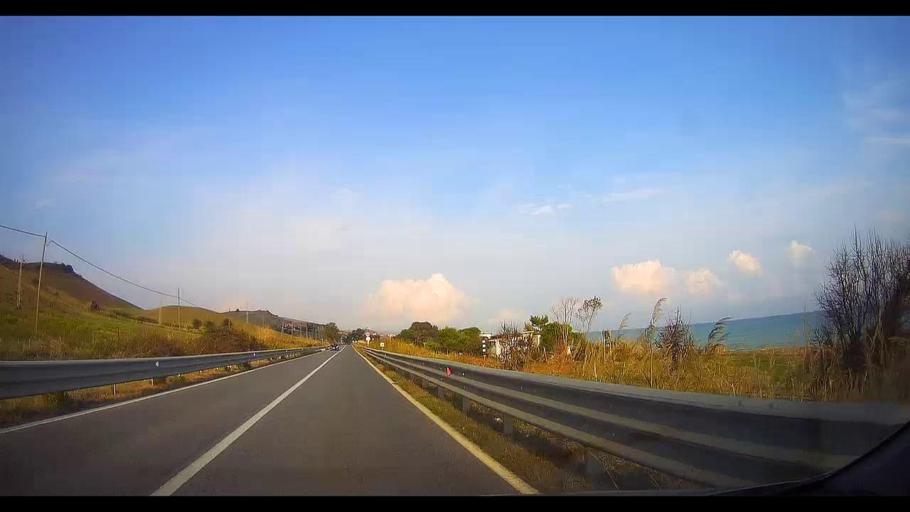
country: IT
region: Calabria
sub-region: Provincia di Cosenza
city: Cariati
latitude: 39.5149
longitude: 16.9173
